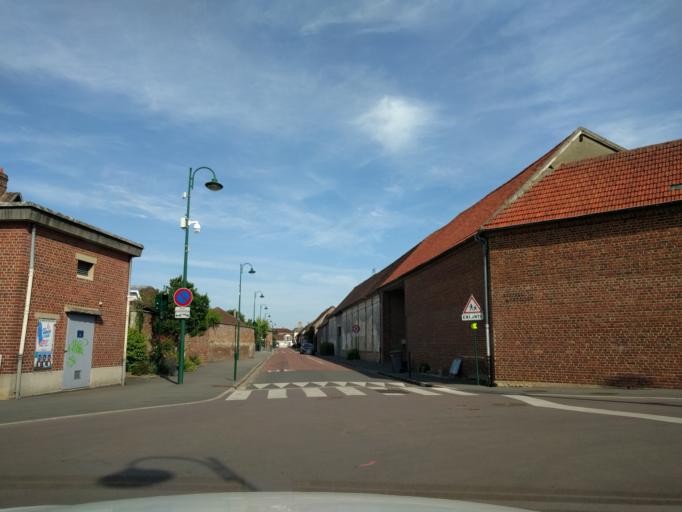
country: FR
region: Picardie
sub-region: Departement de l'Oise
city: Tille
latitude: 49.4645
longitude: 2.1125
